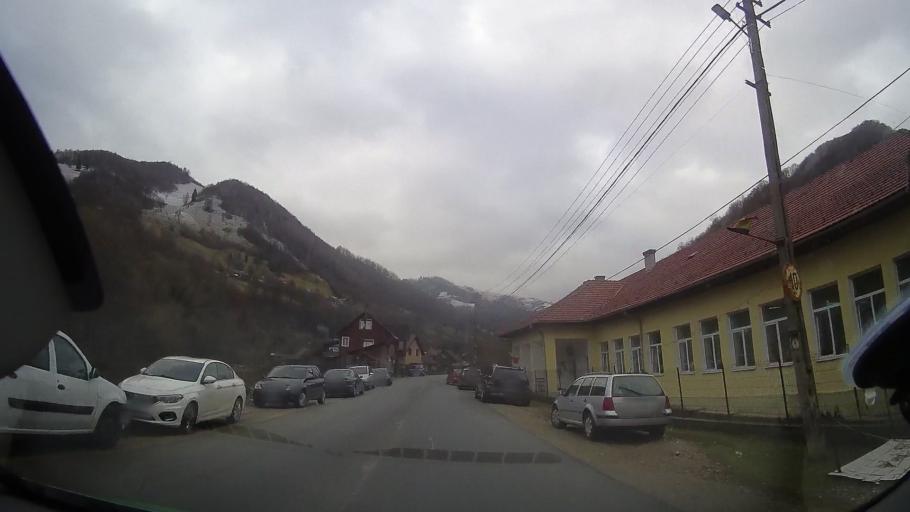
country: RO
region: Cluj
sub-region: Comuna Maguri-Racatau
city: Maguri-Racatau
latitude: 46.6504
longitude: 23.1980
